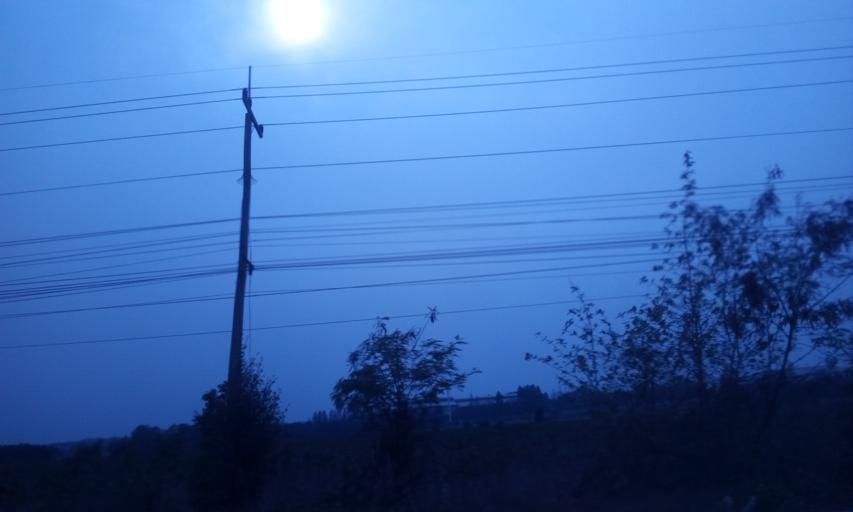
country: TH
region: Chachoengsao
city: Plaeng Yao
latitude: 13.5374
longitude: 101.2629
